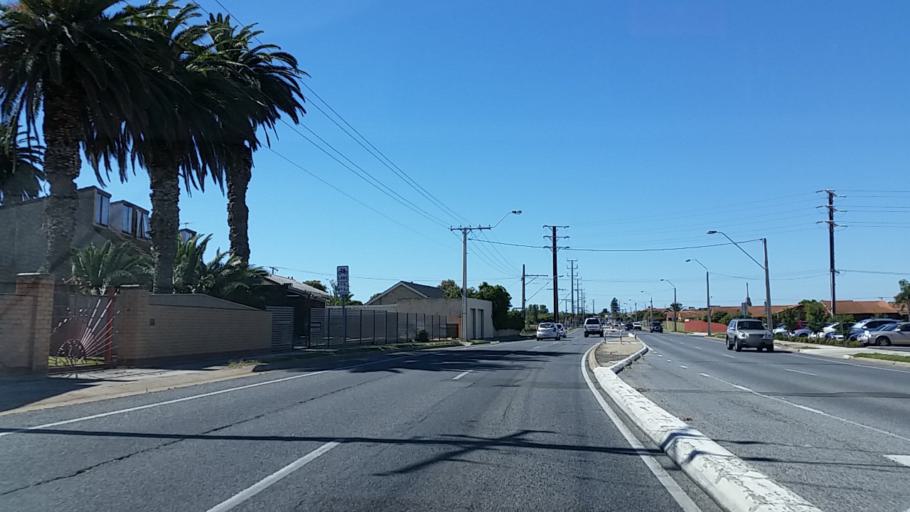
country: AU
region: South Australia
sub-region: Charles Sturt
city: West Lakes Shore
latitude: -34.8570
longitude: 138.4784
